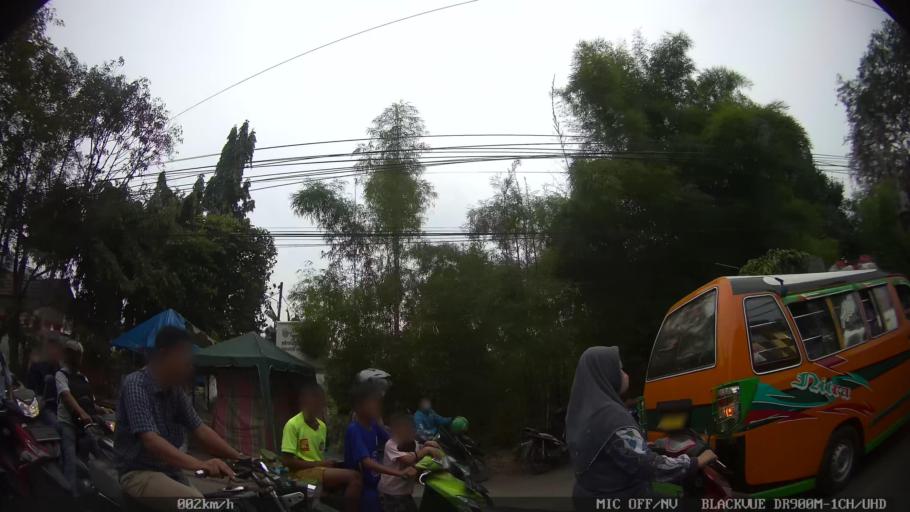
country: ID
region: North Sumatra
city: Medan
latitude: 3.5532
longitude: 98.6917
